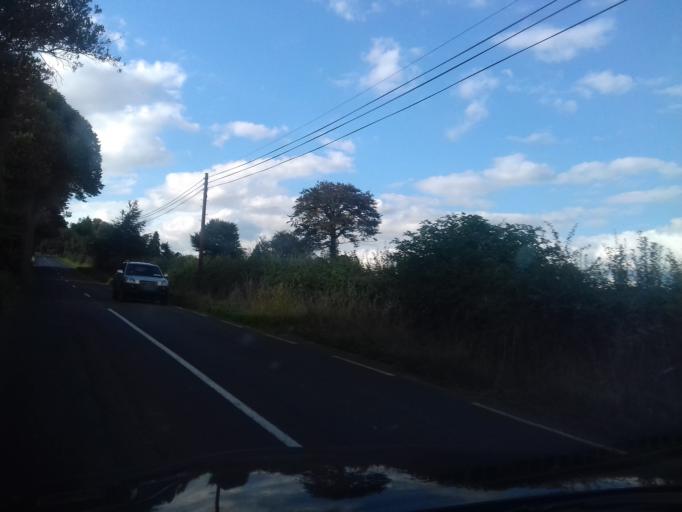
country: IE
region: Leinster
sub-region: Loch Garman
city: New Ross
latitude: 52.4415
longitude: -6.9607
